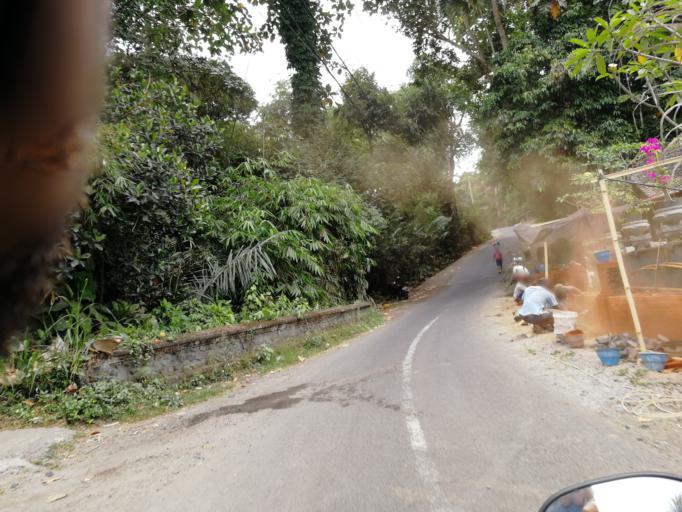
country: ID
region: Bali
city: Banjar Wangsian
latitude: -8.4674
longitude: 115.4459
